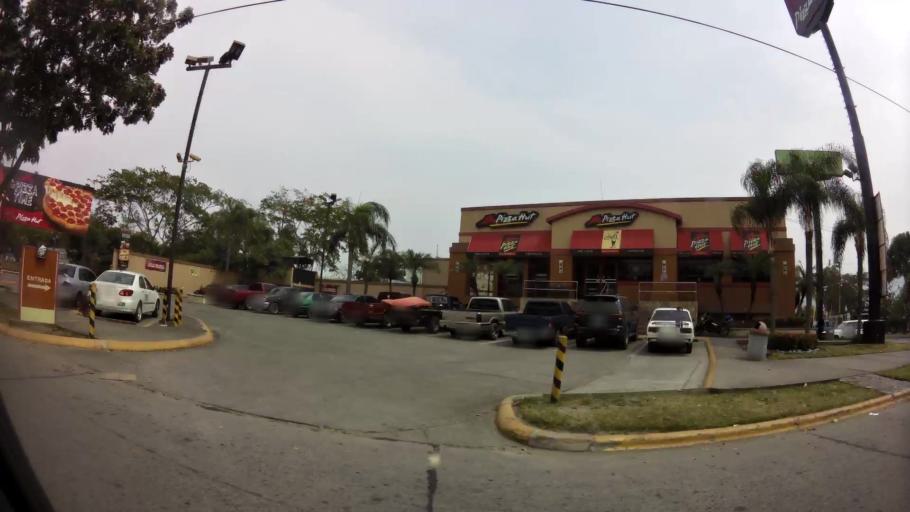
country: HN
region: Cortes
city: San Pedro Sula
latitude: 15.4900
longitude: -88.0189
